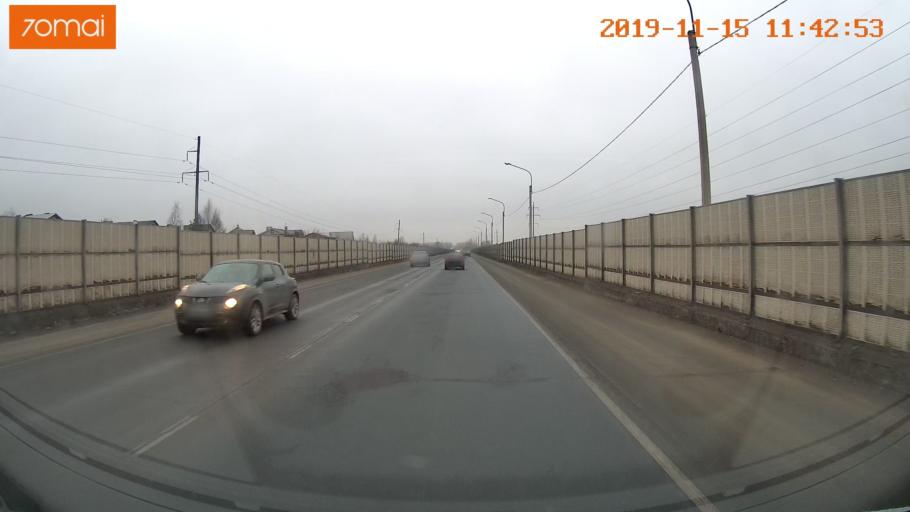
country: RU
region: Vologda
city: Vologda
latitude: 59.2235
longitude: 39.7751
